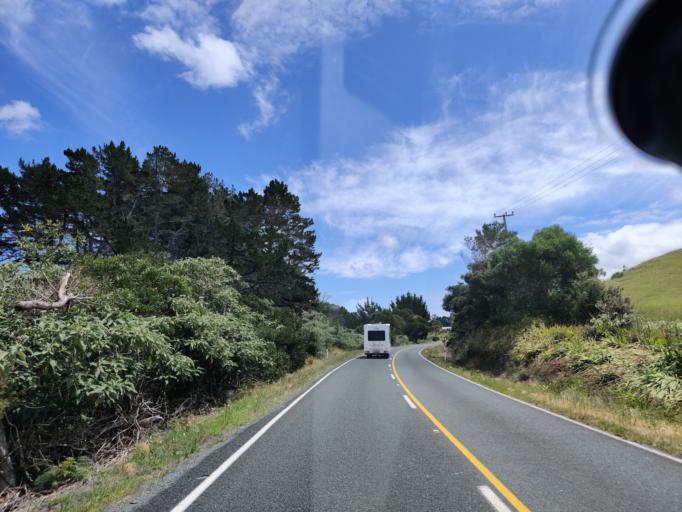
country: NZ
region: Northland
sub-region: Far North District
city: Kaitaia
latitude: -34.7574
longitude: 173.0665
